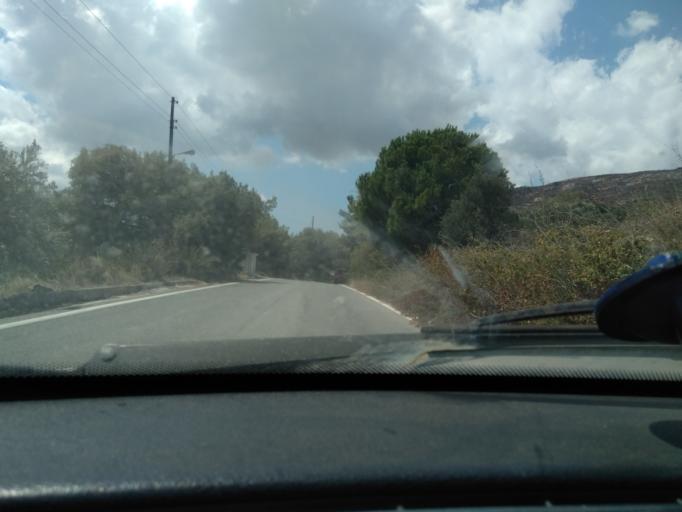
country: GR
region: Crete
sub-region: Nomos Lasithiou
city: Siteia
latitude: 35.1245
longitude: 26.0653
